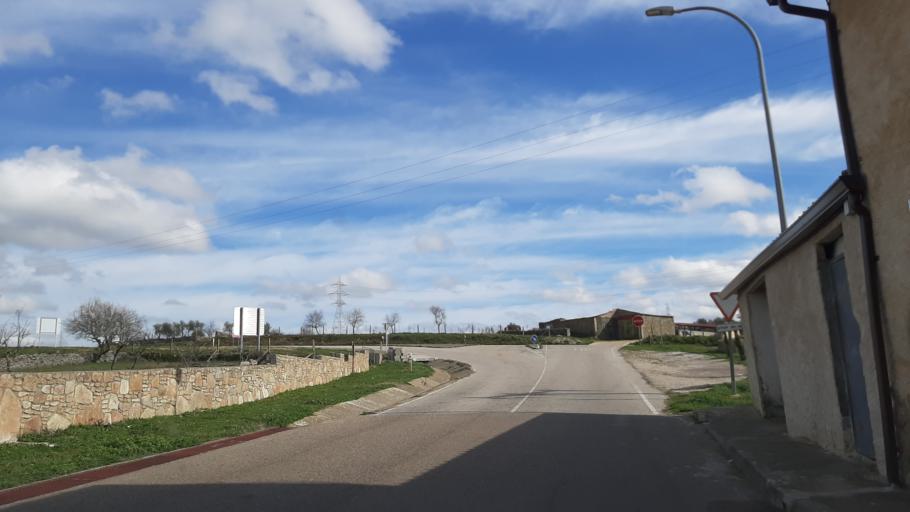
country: ES
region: Castille and Leon
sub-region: Provincia de Salamanca
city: Villarino de los Aires
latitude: 41.2365
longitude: -6.5198
